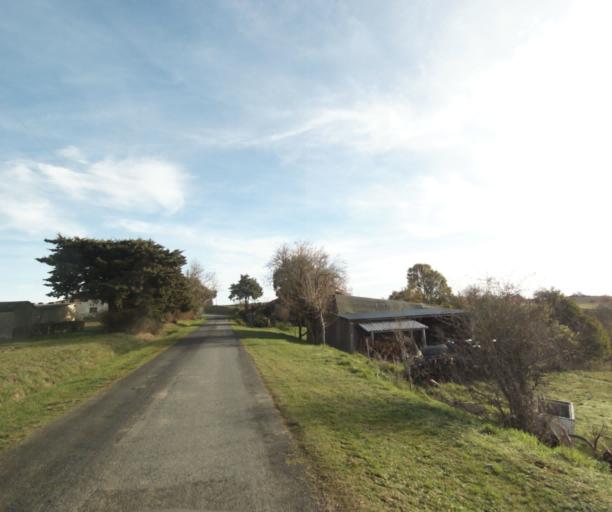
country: FR
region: Midi-Pyrenees
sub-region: Departement de la Haute-Garonne
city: Villemur-sur-Tarn
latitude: 43.8541
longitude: 1.5204
